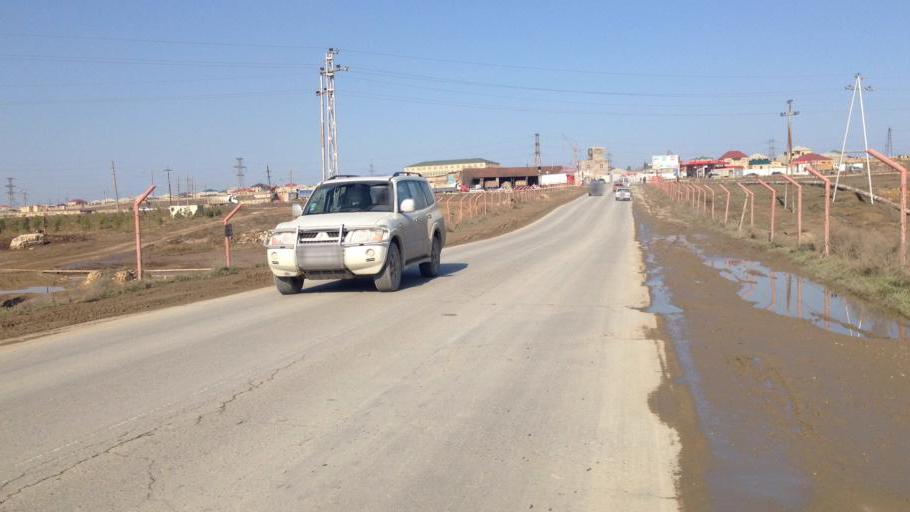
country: AZ
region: Abseron
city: Digah
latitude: 40.4781
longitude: 49.8561
